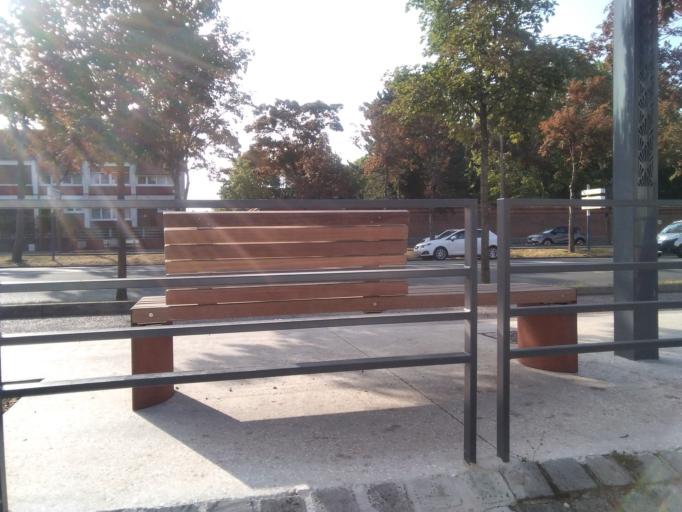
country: FR
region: Picardie
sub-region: Departement de la Somme
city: Rivery
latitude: 49.9060
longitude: 2.3174
